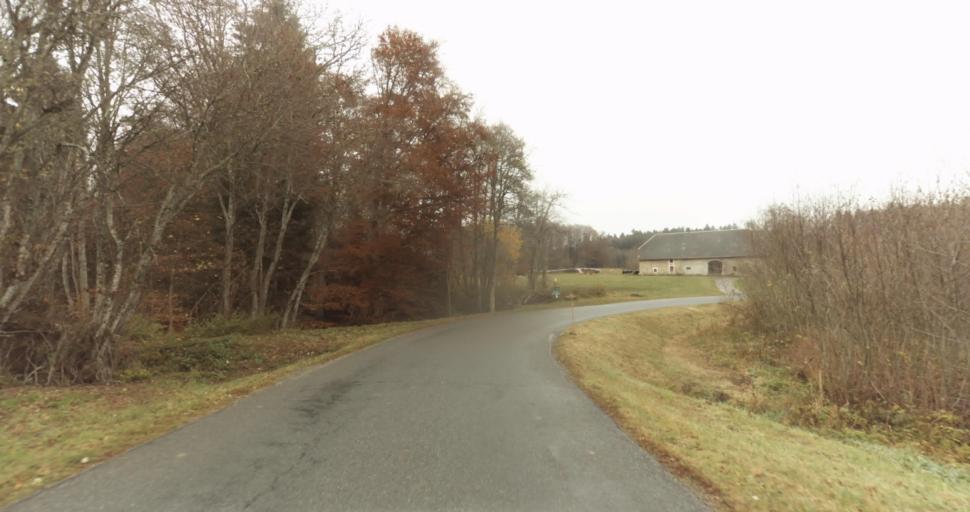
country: FR
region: Rhone-Alpes
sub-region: Departement de la Haute-Savoie
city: Evires
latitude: 46.0665
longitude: 6.2117
